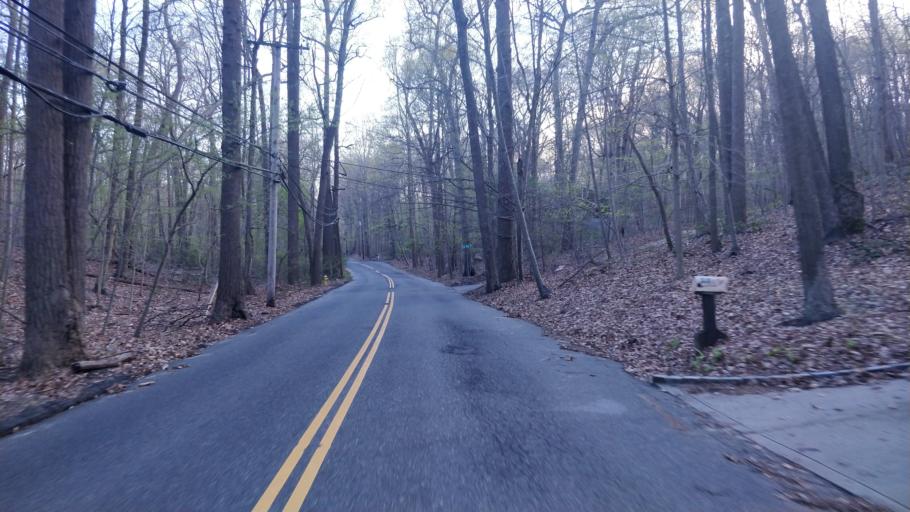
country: US
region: New York
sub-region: Suffolk County
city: Village of the Branch
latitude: 40.8805
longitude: -73.1858
